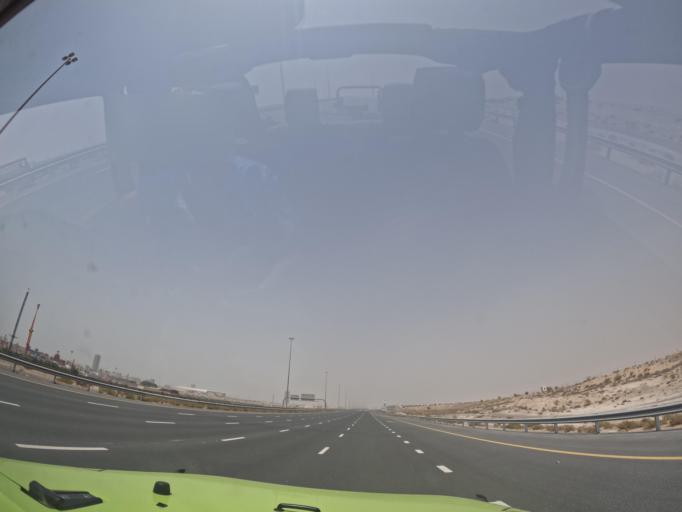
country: AE
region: Dubai
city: Dubai
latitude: 25.0625
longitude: 55.3072
